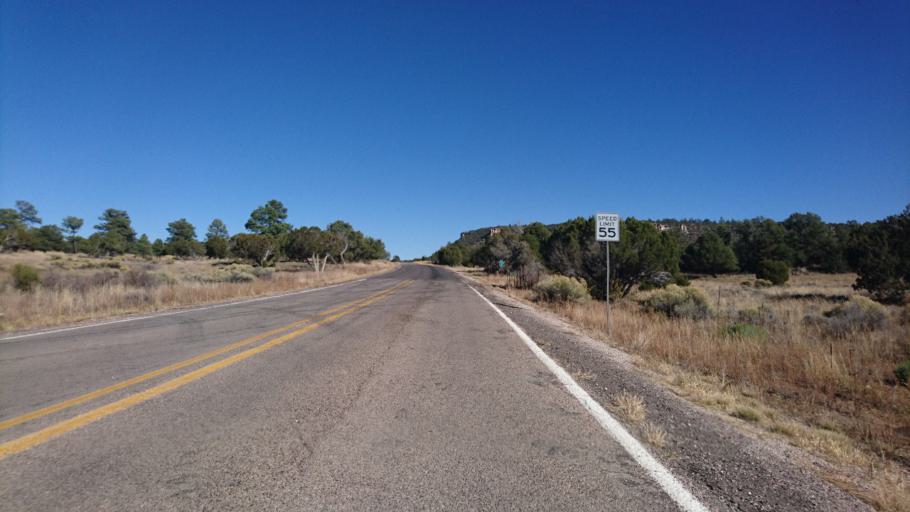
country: US
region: New Mexico
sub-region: McKinley County
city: Thoreau
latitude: 35.0431
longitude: -108.3364
